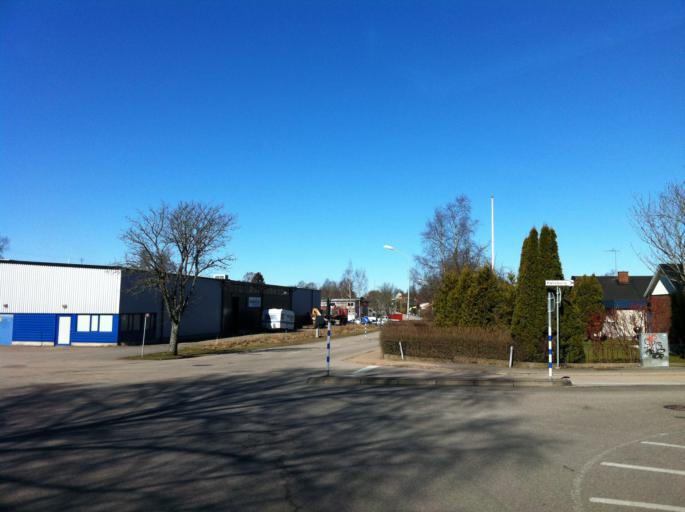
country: SE
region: Vaestra Goetaland
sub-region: Vanersborgs Kommun
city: Vargon
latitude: 58.3513
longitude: 12.4088
